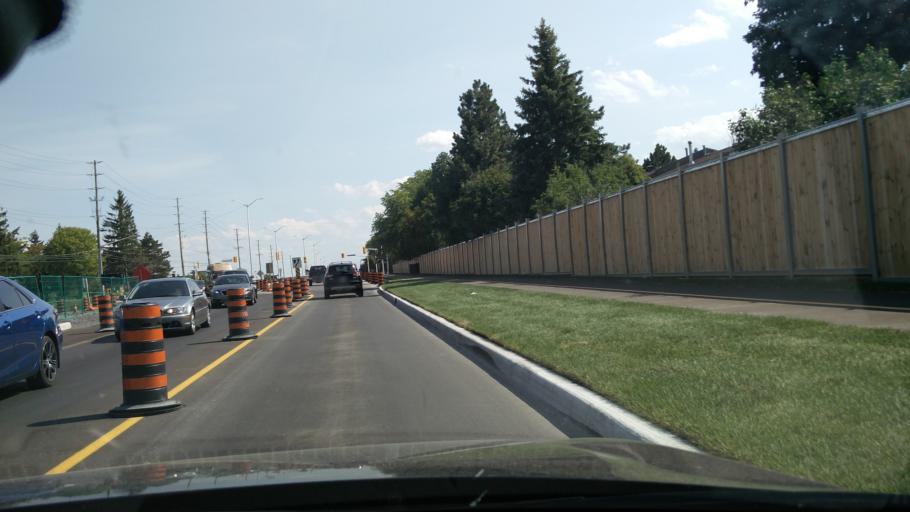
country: CA
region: Ontario
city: Bells Corners
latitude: 45.2765
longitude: -75.7500
